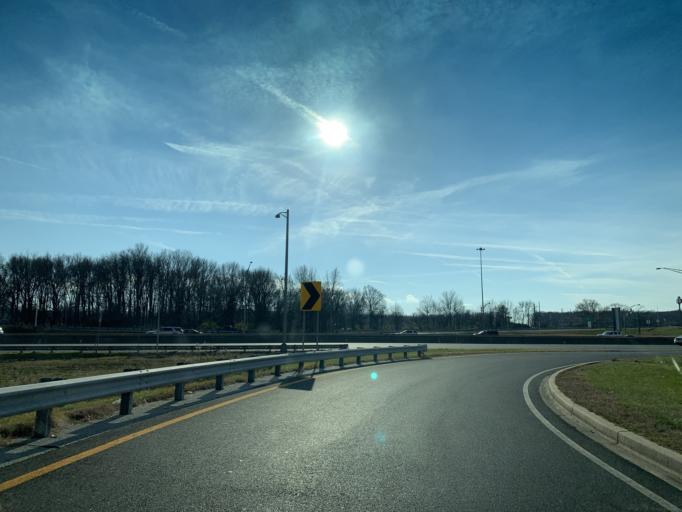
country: US
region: New Jersey
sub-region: Salem County
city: Carneys Point
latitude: 39.6802
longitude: -75.4908
